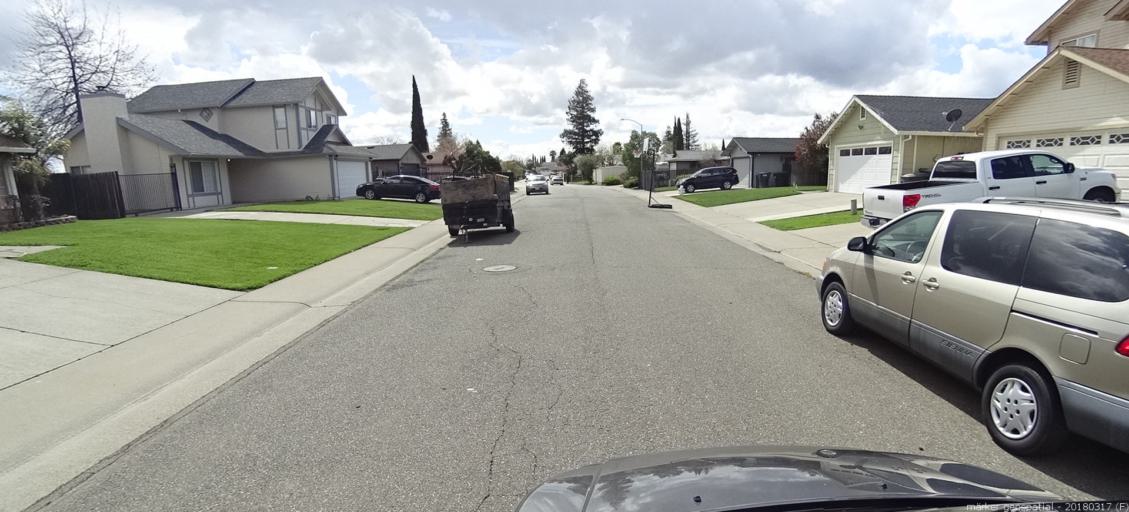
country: US
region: California
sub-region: Sacramento County
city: Florin
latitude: 38.4786
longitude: -121.4061
